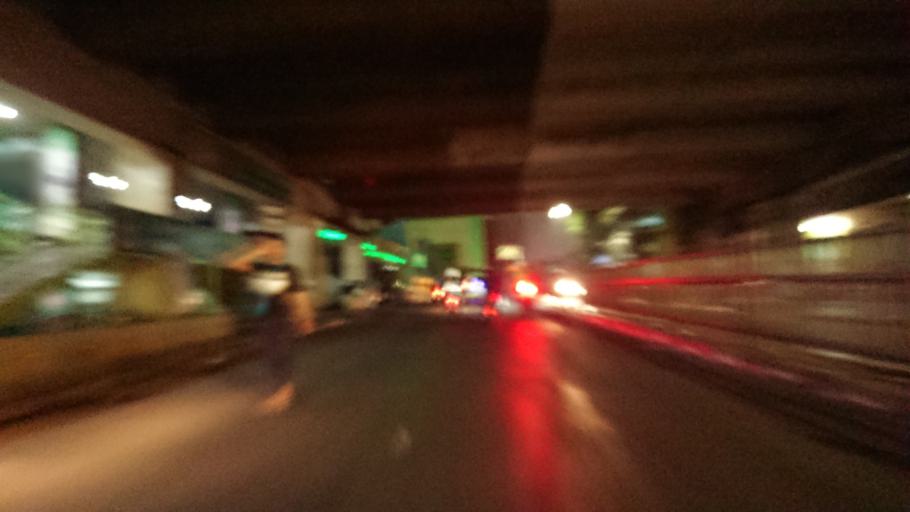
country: ID
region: Jakarta Raya
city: Jakarta
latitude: -6.1884
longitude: 106.8145
